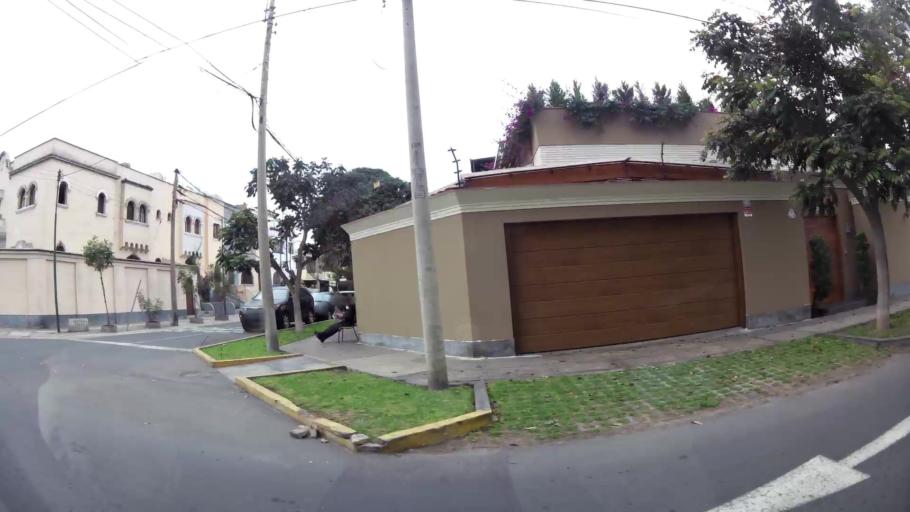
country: PE
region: Lima
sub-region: Lima
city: Surco
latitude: -12.1234
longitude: -77.0211
